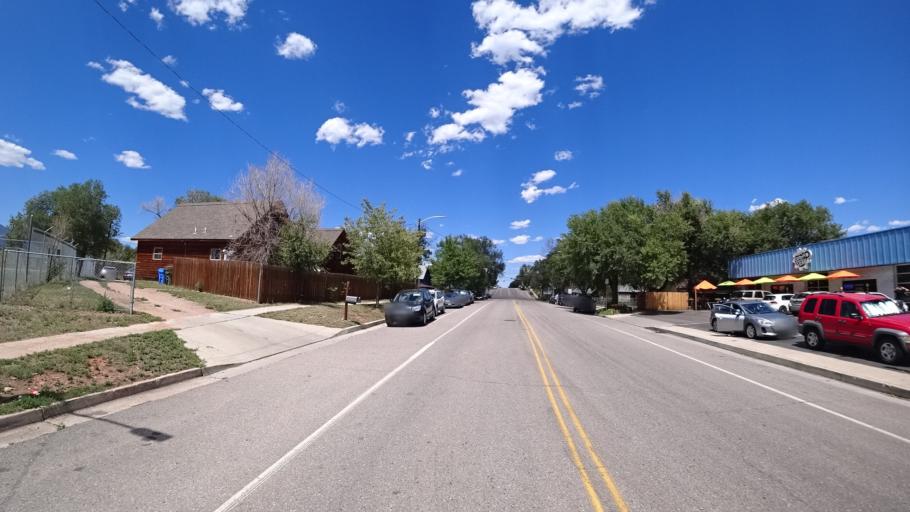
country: US
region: Colorado
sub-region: El Paso County
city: Colorado Springs
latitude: 38.8189
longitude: -104.8297
